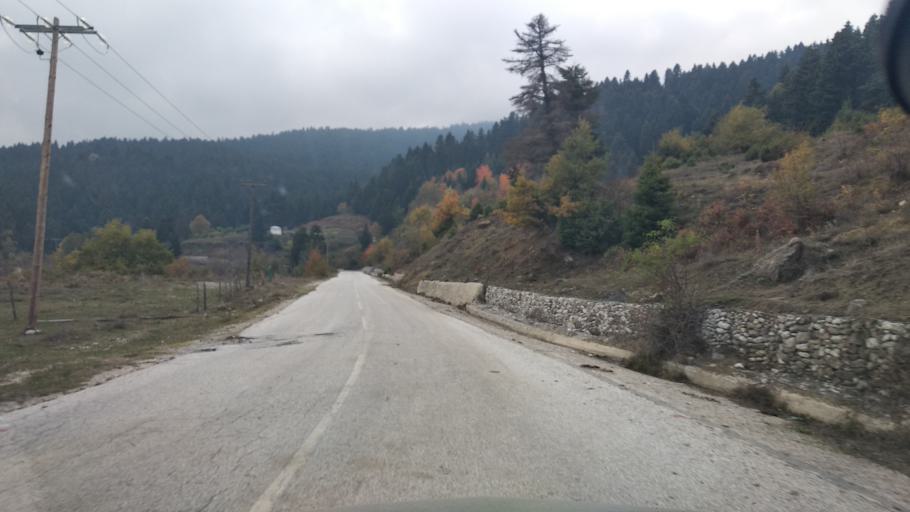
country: GR
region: Thessaly
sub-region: Trikala
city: Fiki
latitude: 39.5855
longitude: 21.4919
